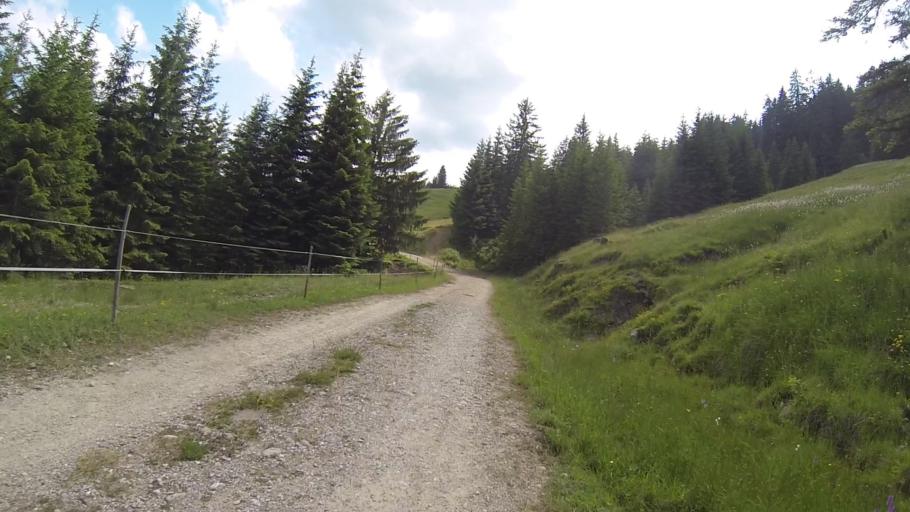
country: AT
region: Tyrol
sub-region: Politischer Bezirk Reutte
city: Jungholz
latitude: 47.5847
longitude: 10.4684
